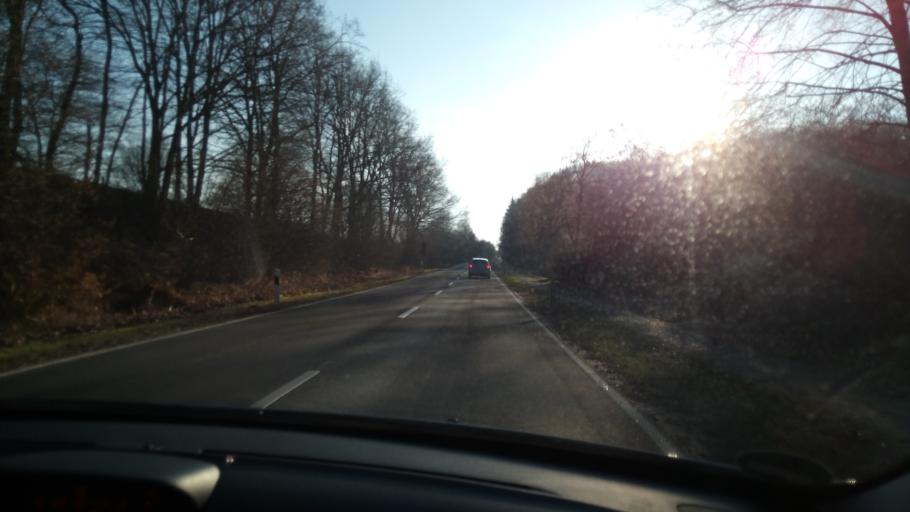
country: DE
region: Schleswig-Holstein
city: Buchen
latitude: 53.4684
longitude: 10.6237
